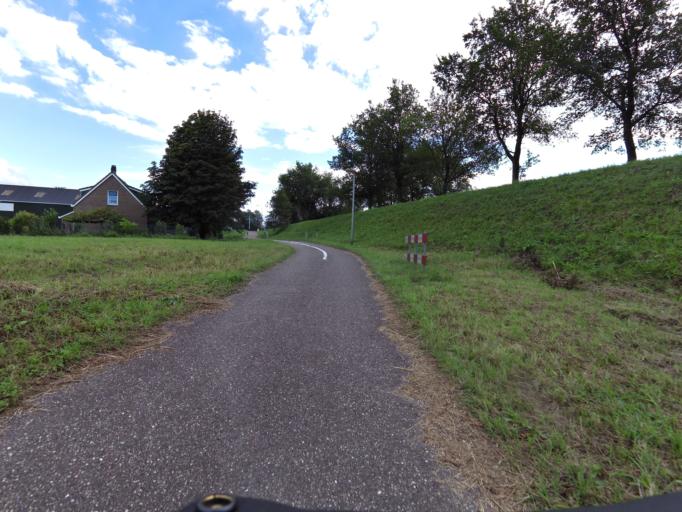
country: NL
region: North Brabant
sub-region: Gemeente Steenbergen
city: Nieuw-Vossemeer
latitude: 51.6939
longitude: 4.2674
